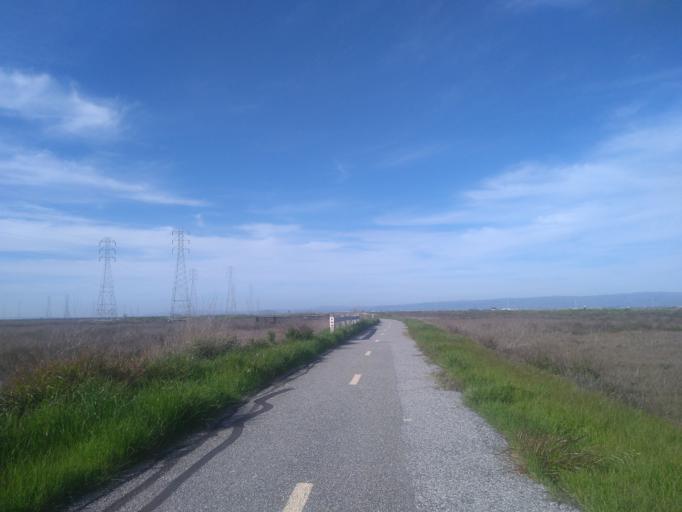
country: US
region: California
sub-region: Santa Clara County
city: Mountain View
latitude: 37.4326
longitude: -122.0684
